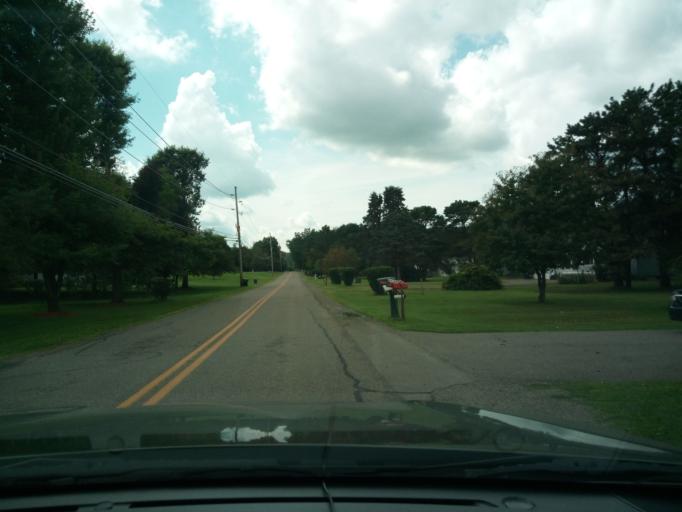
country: US
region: Pennsylvania
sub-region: Bradford County
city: South Waverly
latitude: 41.9960
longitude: -76.5738
